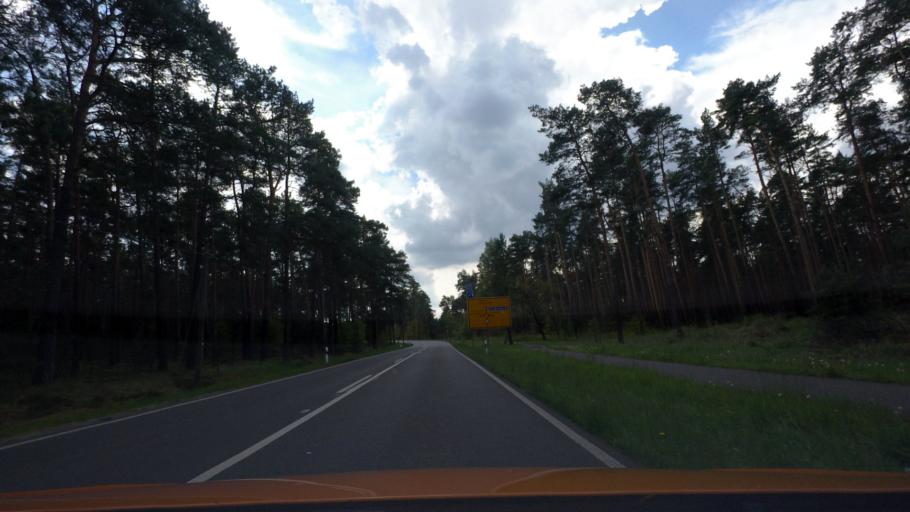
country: DE
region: Brandenburg
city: Grunheide
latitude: 52.3945
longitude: 13.8249
